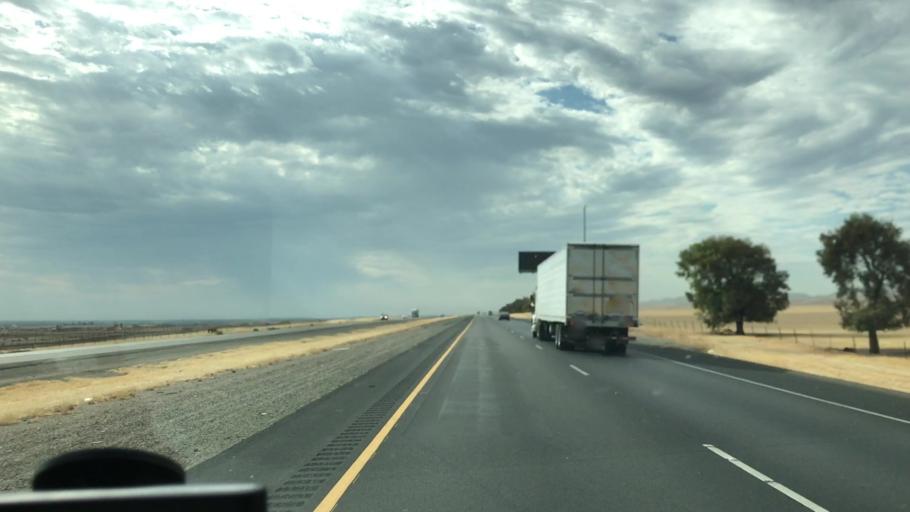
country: US
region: California
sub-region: San Joaquin County
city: Tracy
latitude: 37.6802
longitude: -121.4711
